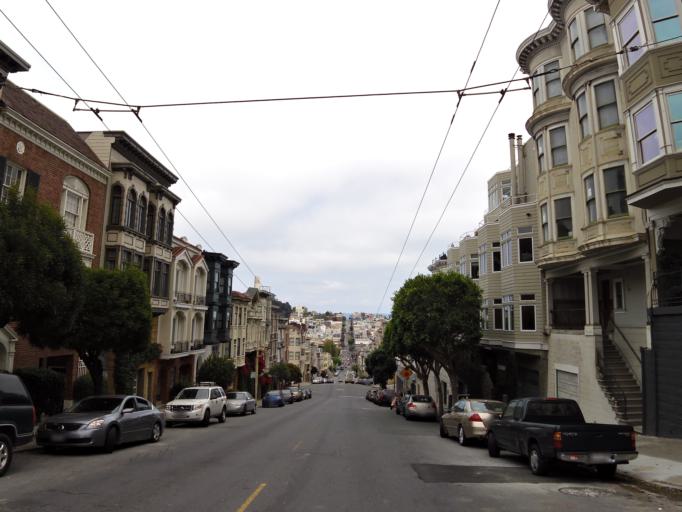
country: US
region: California
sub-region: San Francisco County
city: San Francisco
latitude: 37.7997
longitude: -122.4153
